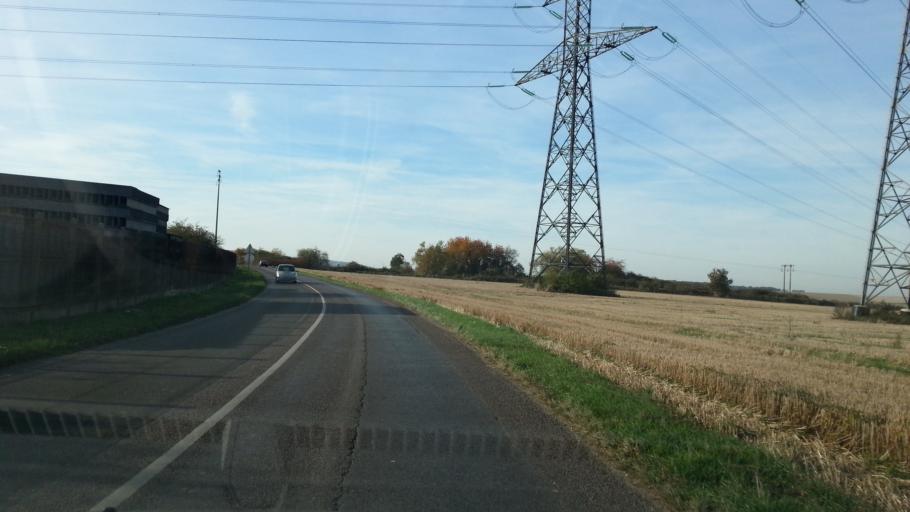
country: FR
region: Ile-de-France
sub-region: Departement du Val-d'Oise
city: Persan
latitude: 49.1662
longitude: 2.2764
